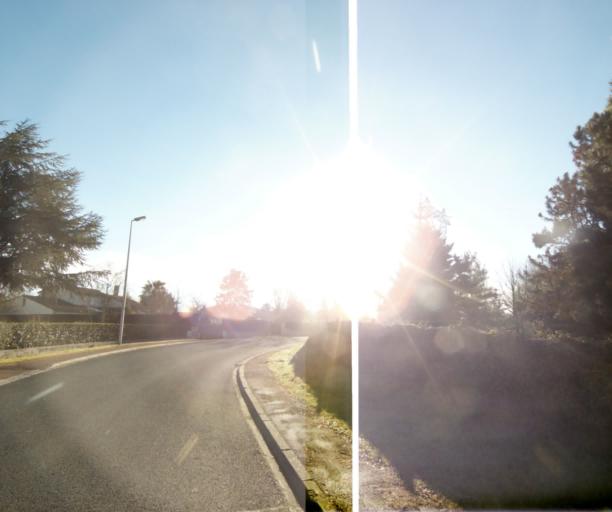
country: FR
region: Poitou-Charentes
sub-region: Departement de la Charente-Maritime
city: Fontcouverte
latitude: 45.7687
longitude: -0.5902
